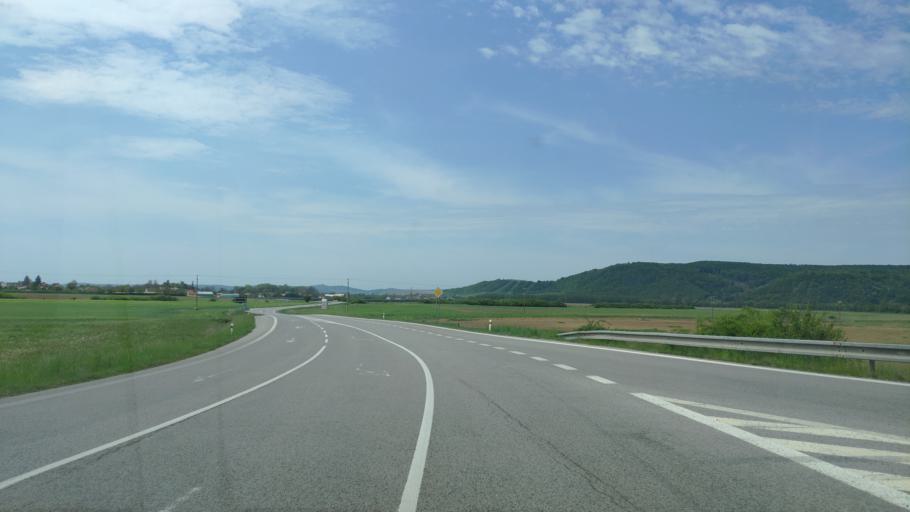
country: HU
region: Borsod-Abauj-Zemplen
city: Putnok
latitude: 48.4487
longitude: 20.3408
